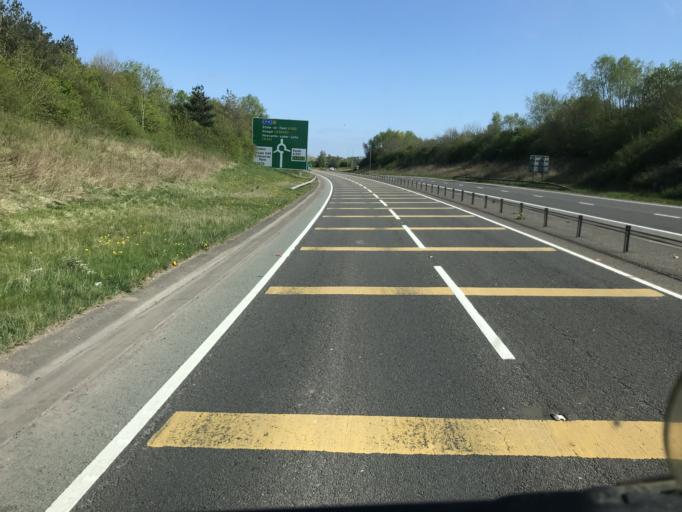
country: GB
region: England
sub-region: Cheshire East
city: Weston
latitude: 53.0686
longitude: -2.3876
